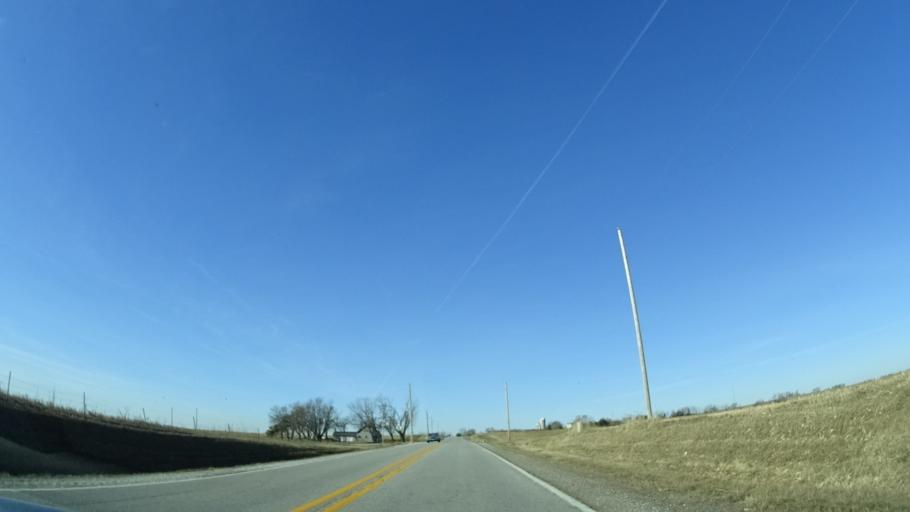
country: US
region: Nebraska
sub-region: Sarpy County
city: Papillion
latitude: 41.0891
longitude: -96.0644
